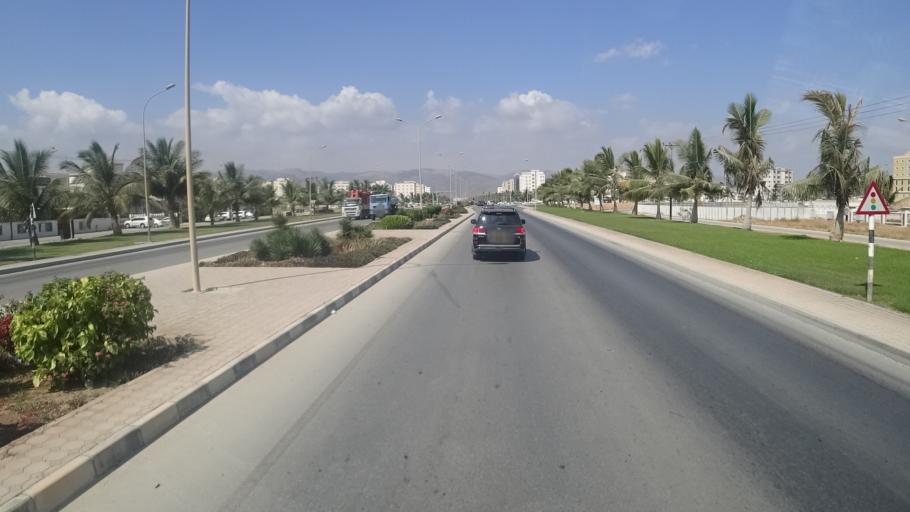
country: OM
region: Zufar
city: Salalah
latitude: 17.0183
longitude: 54.0349
